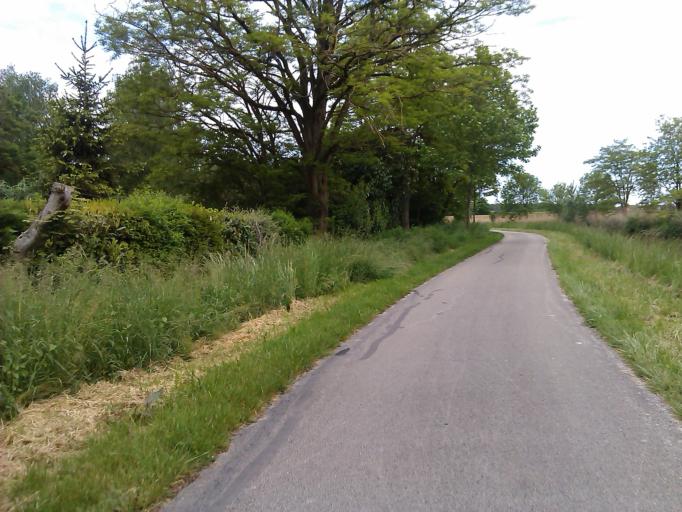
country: FR
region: Bourgogne
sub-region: Departement de Saone-et-Loire
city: Champforgeuil
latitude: 46.8391
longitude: 4.8280
